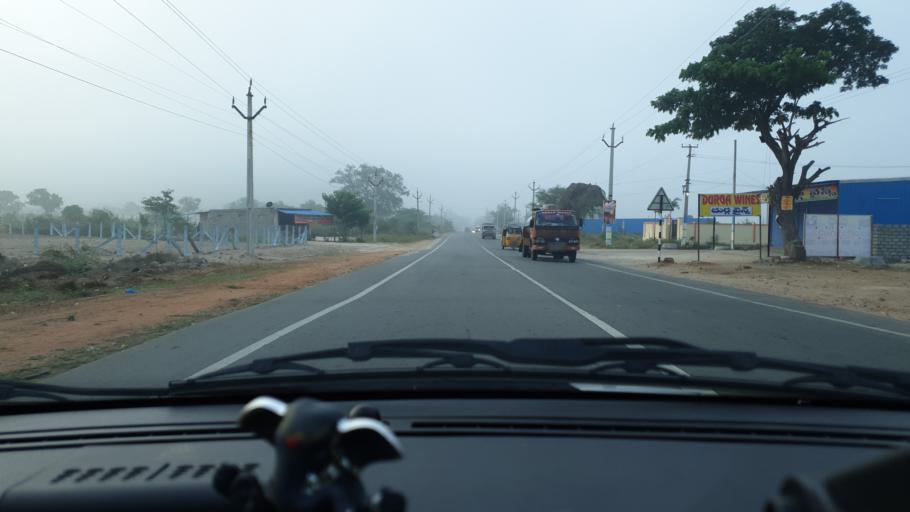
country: IN
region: Telangana
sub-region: Mahbubnagar
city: Farrukhnagar
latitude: 16.8772
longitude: 78.5293
